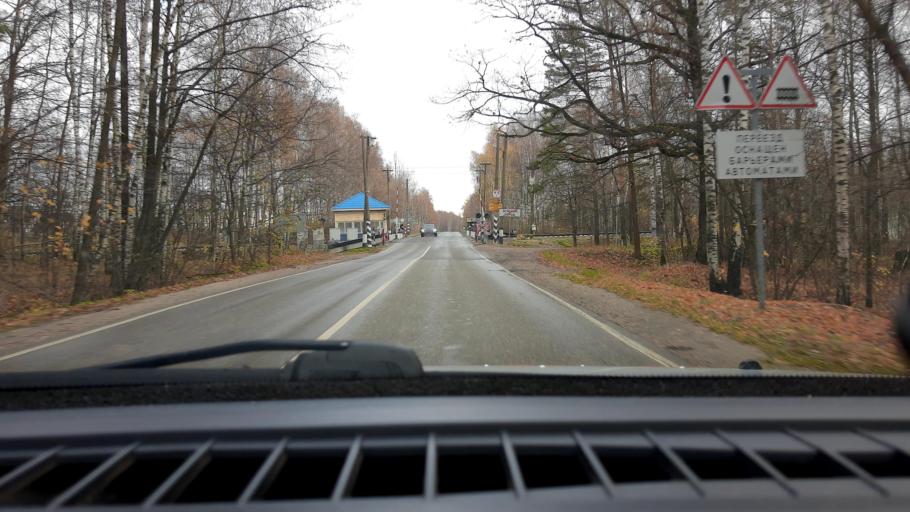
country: RU
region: Nizjnij Novgorod
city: Afonino
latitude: 56.1870
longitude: 44.1142
